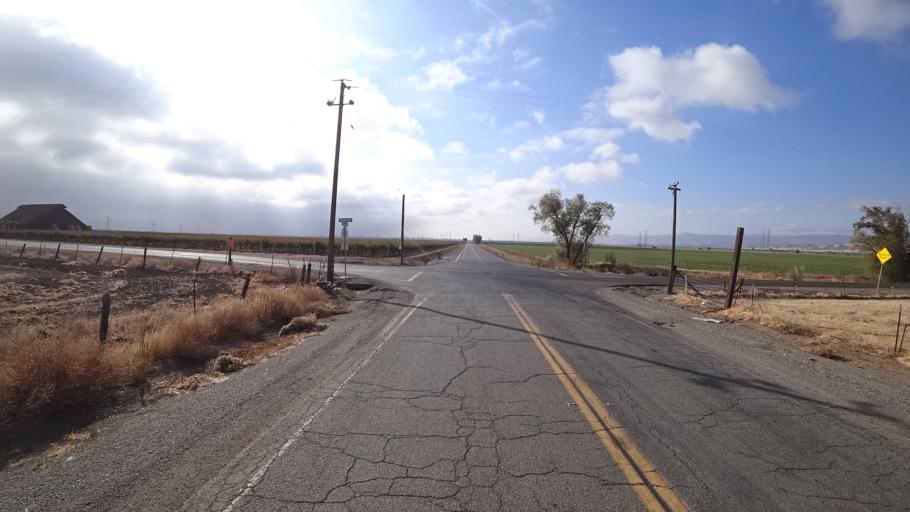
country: US
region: California
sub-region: Yolo County
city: Esparto
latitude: 38.7811
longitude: -122.0073
